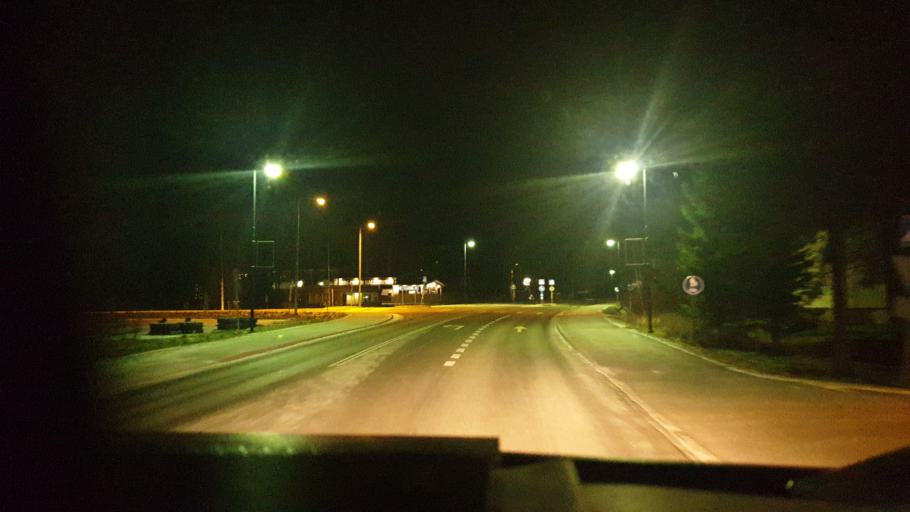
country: FI
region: Southern Ostrobothnia
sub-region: Kuusiokunnat
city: Toeysae
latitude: 62.6041
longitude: 23.7388
